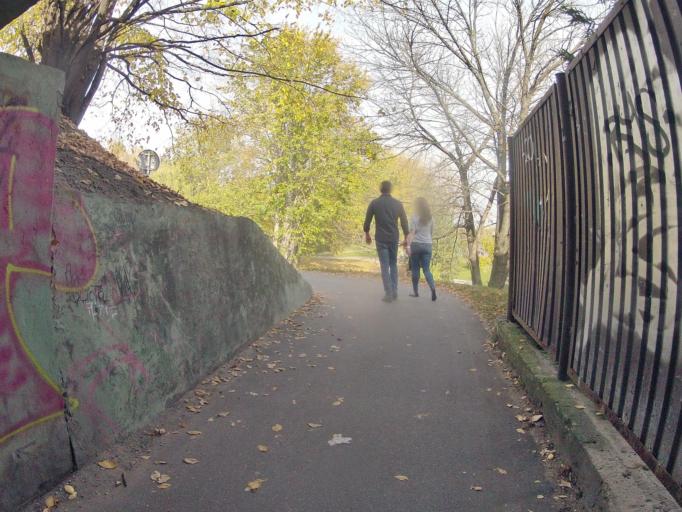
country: PL
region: Lesser Poland Voivodeship
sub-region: Krakow
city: Krakow
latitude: 50.0544
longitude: 19.9764
